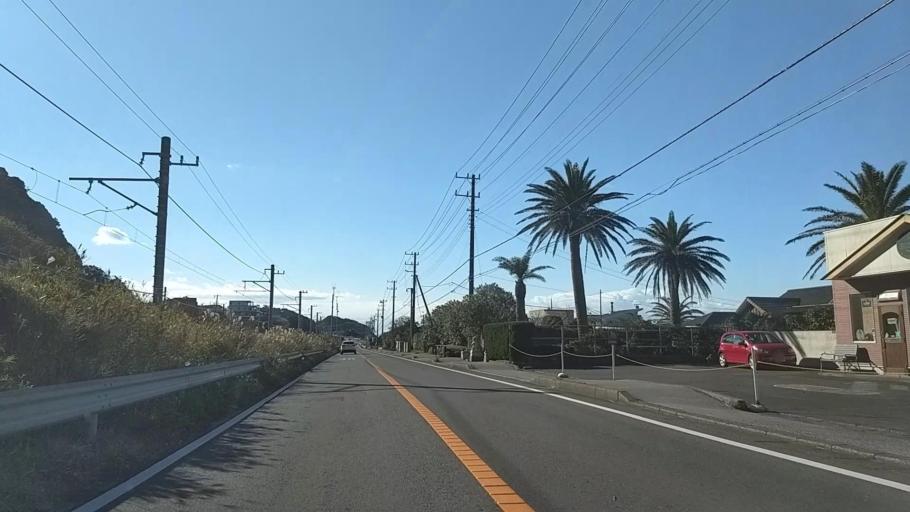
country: JP
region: Chiba
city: Futtsu
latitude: 35.1889
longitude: 139.8198
